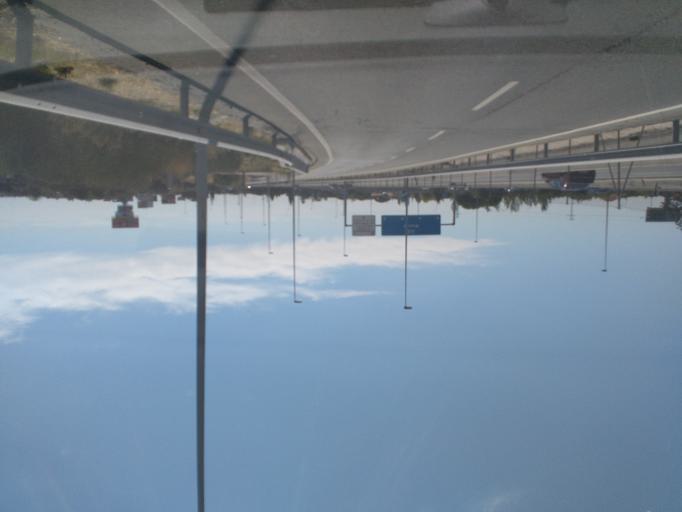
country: ES
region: Madrid
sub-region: Provincia de Madrid
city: Las Matas
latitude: 40.5621
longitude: -3.9042
